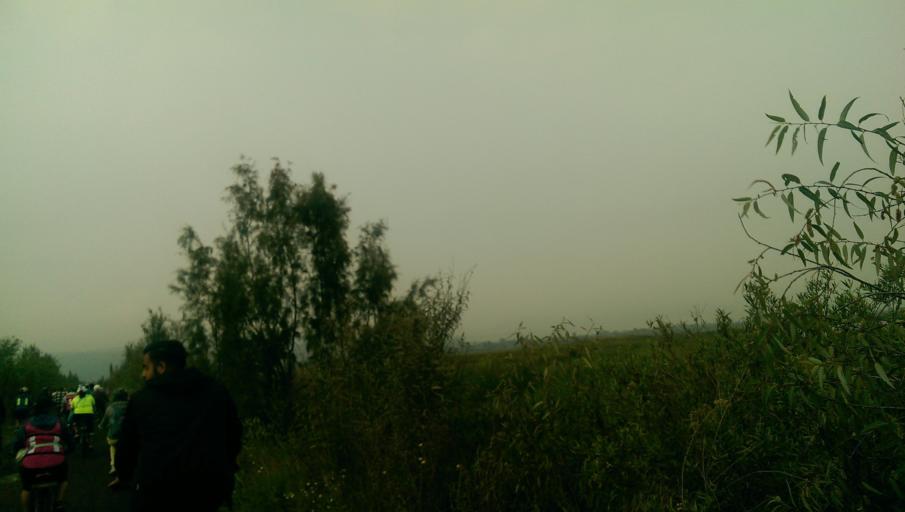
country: MX
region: Mexico City
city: Tlahuac
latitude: 19.2697
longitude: -99.0443
